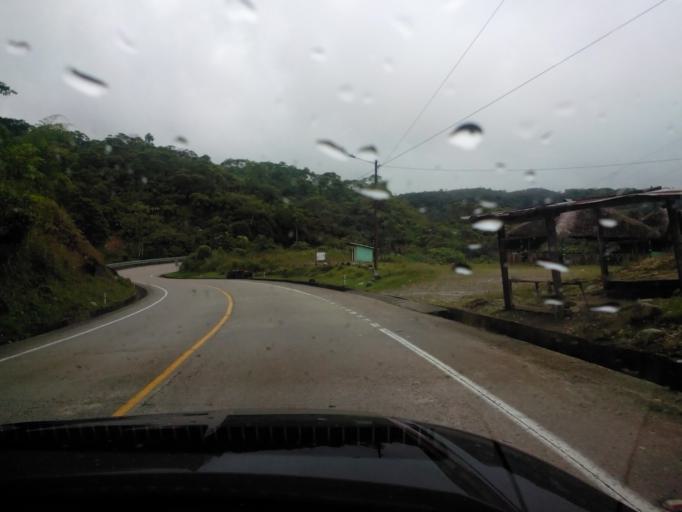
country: EC
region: Napo
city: Archidona
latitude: -0.7914
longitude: -77.7797
